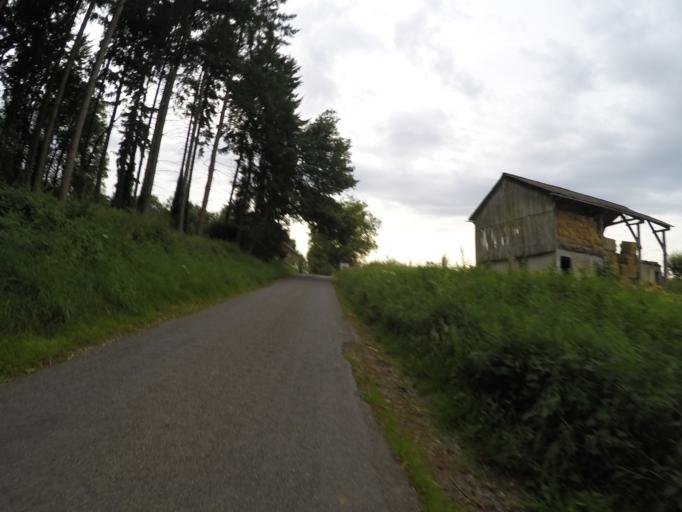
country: BE
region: Wallonia
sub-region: Province de Namur
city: Assesse
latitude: 50.3299
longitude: 5.0359
